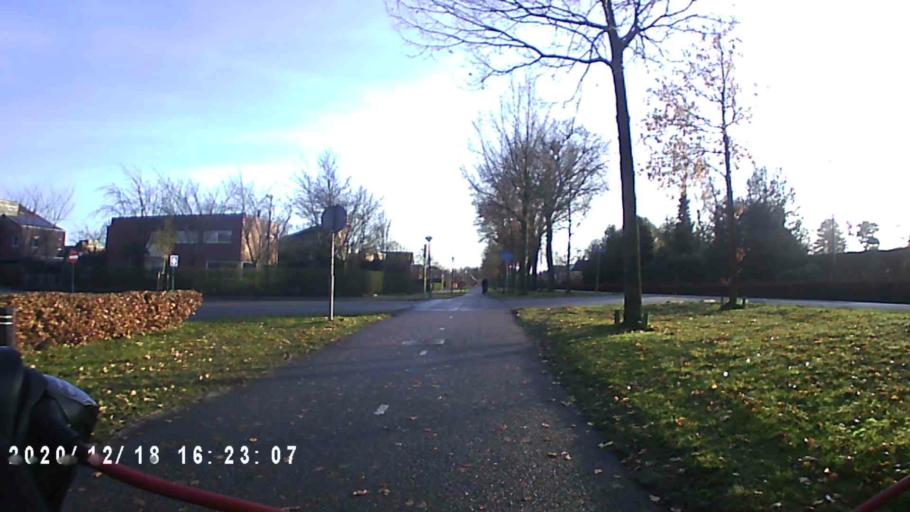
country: NL
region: Drenthe
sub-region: Gemeente Tynaarlo
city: Zuidlaren
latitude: 53.0903
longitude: 6.6916
